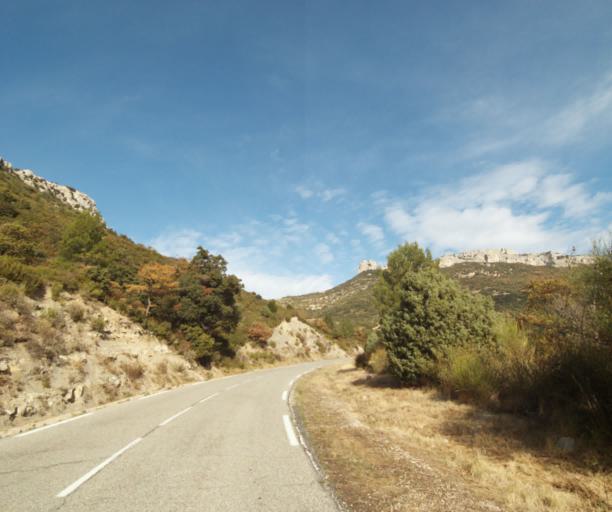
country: FR
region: Provence-Alpes-Cote d'Azur
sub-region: Departement des Bouches-du-Rhone
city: Gemenos
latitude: 43.3090
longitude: 5.6643
